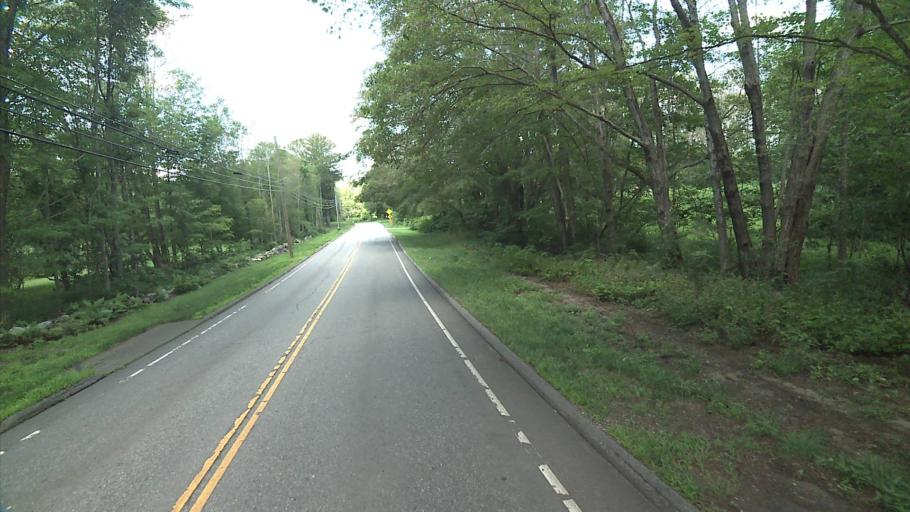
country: US
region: Connecticut
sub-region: Windham County
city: Windham
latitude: 41.6987
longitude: -72.1351
